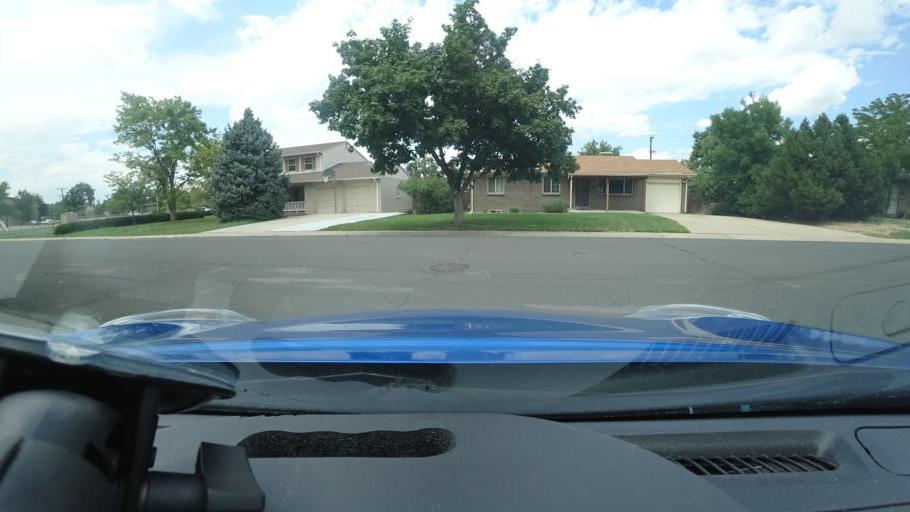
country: US
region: Colorado
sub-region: Adams County
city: Aurora
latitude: 39.7250
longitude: -104.8333
